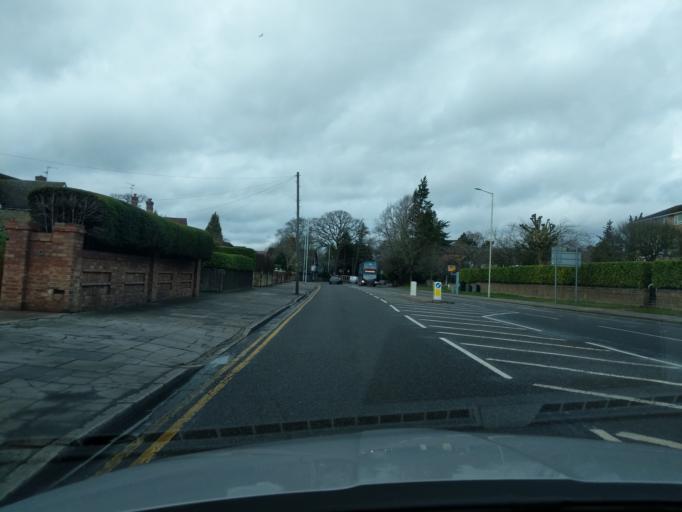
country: GB
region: England
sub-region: Hertfordshire
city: Watford
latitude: 51.6699
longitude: -0.4140
